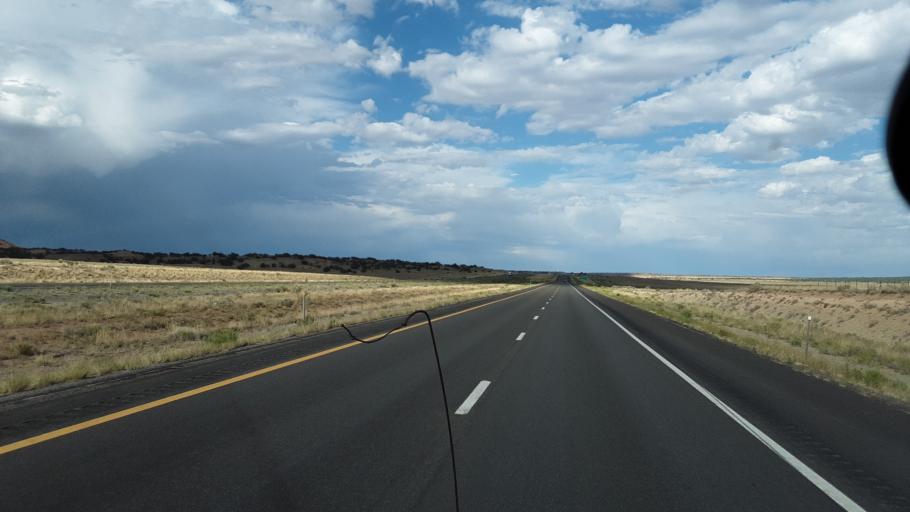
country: US
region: Utah
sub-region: Emery County
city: Castle Dale
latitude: 38.8718
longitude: -110.6850
